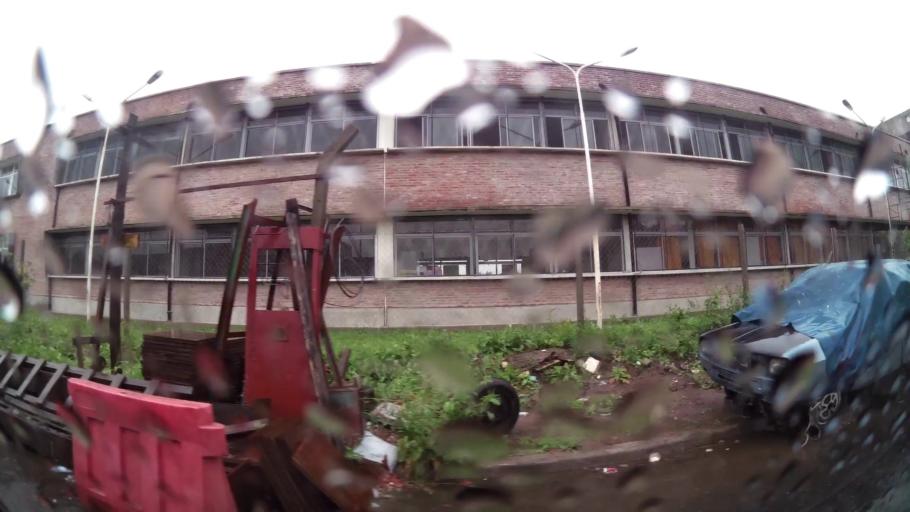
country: AR
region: Buenos Aires F.D.
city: Villa Lugano
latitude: -34.6632
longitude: -58.4504
